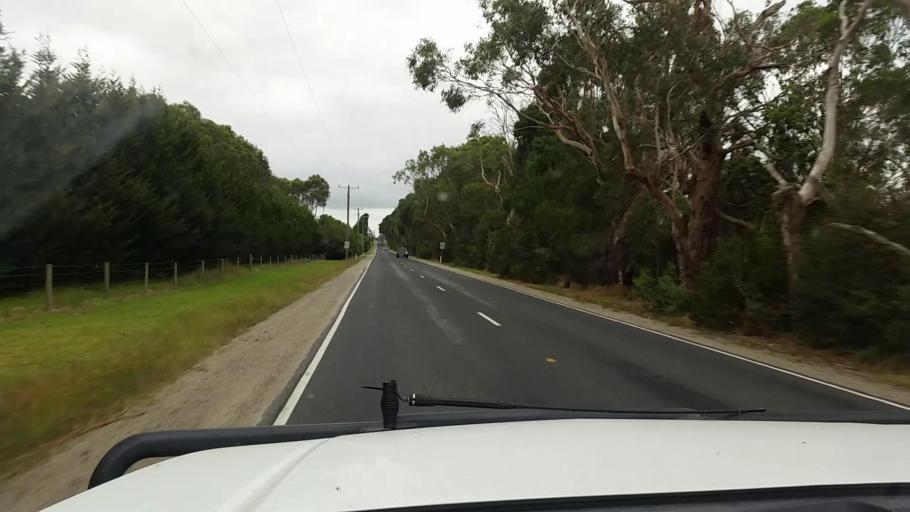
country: AU
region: Victoria
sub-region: Mornington Peninsula
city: Tyabb
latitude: -38.2684
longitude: 145.1456
